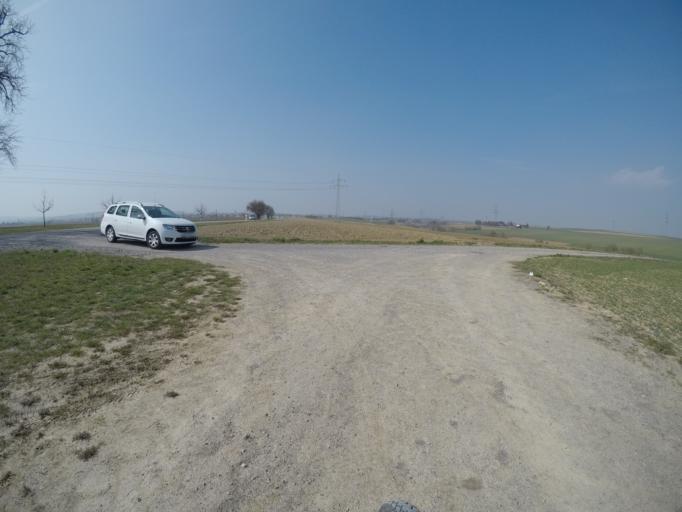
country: DE
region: Baden-Wuerttemberg
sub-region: Regierungsbezirk Stuttgart
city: Herrenberg
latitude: 48.6173
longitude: 8.8648
